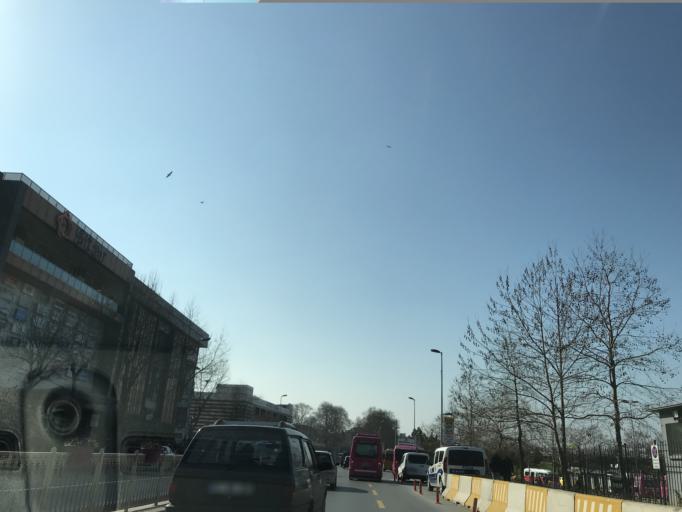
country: TR
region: Yalova
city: Yalova
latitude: 40.6592
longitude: 29.2779
